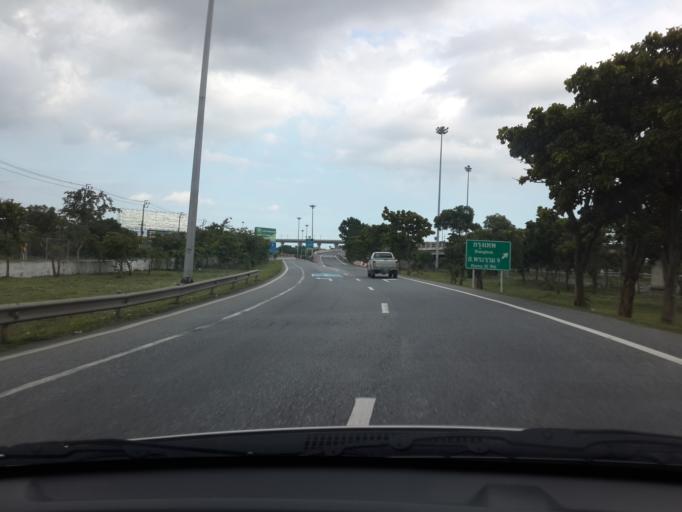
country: TH
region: Bangkok
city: Saphan Sung
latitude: 13.7356
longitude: 100.7034
